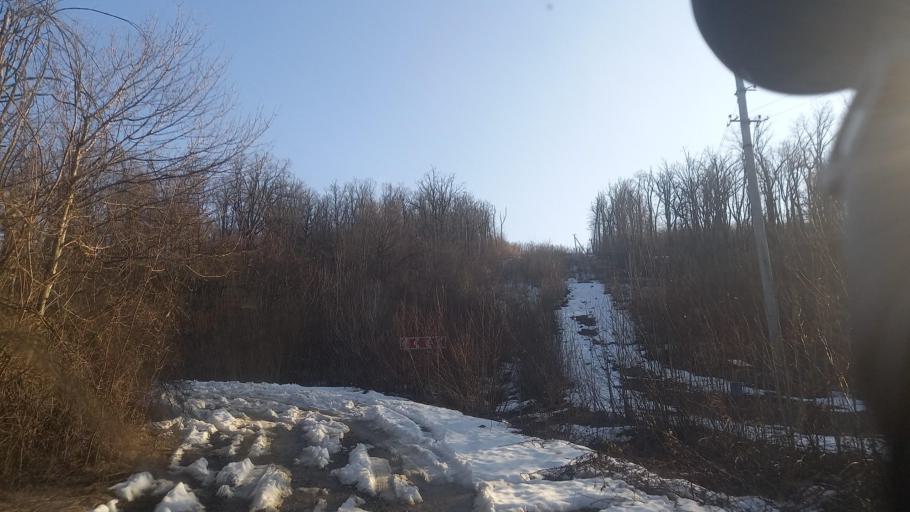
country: RU
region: Krasnodarskiy
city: Smolenskaya
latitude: 44.6693
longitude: 38.7961
